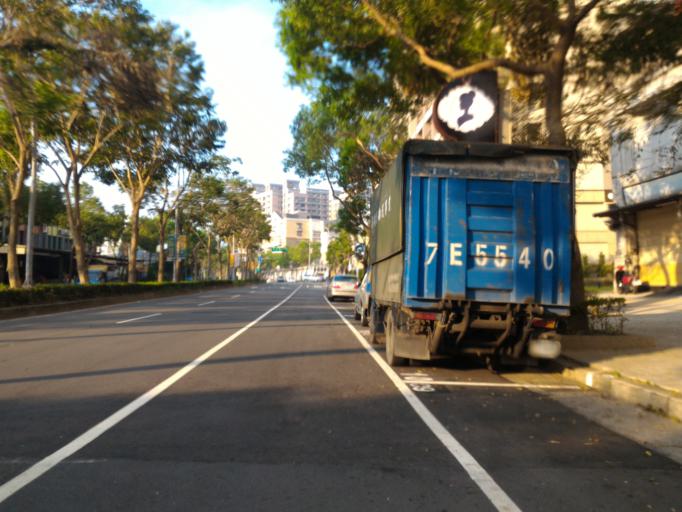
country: TW
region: Taiwan
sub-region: Taoyuan
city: Taoyuan
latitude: 24.9498
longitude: 121.3858
